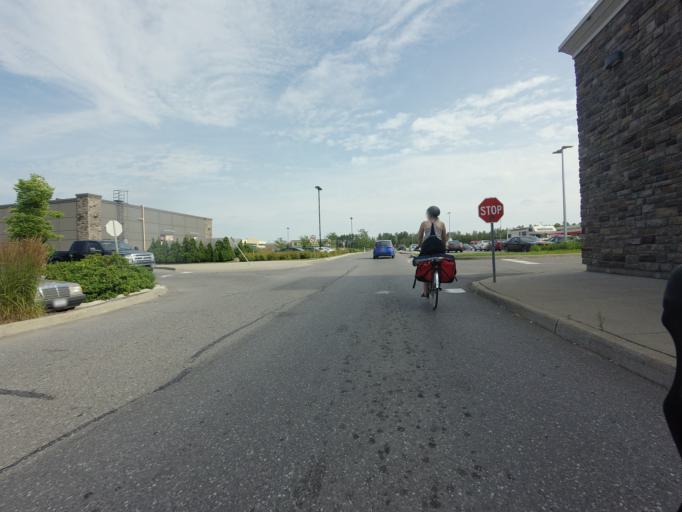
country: CA
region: Ontario
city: Prescott
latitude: 45.0295
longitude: -75.6335
